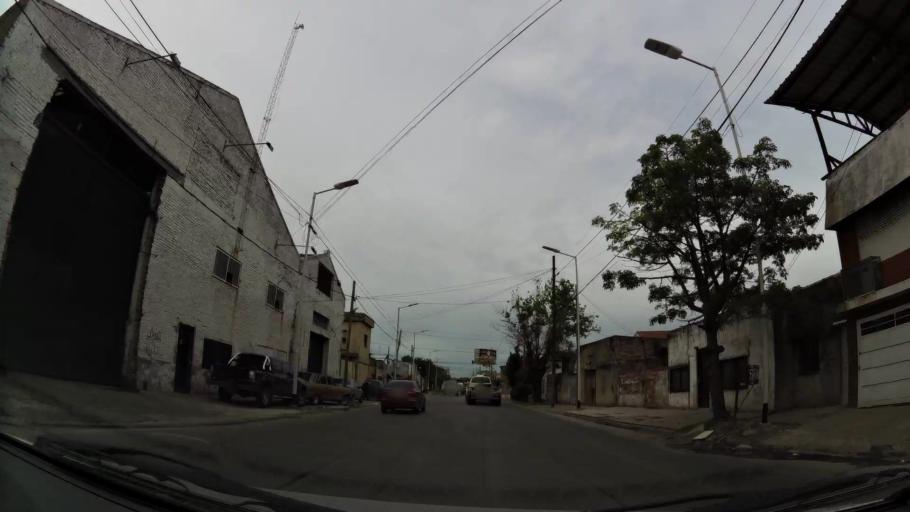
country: AR
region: Buenos Aires
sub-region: Partido de Avellaneda
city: Avellaneda
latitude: -34.6572
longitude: -58.3479
